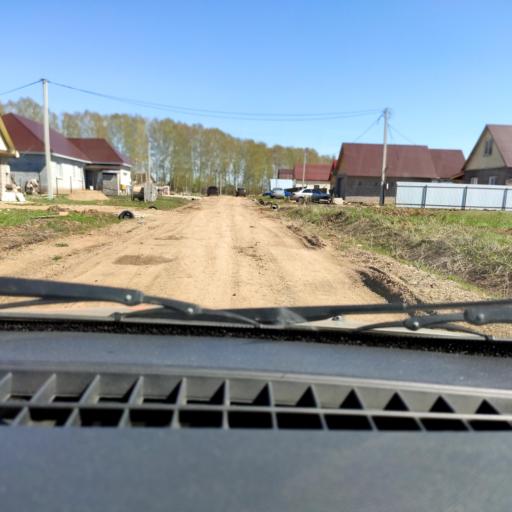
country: RU
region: Bashkortostan
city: Iglino
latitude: 54.8141
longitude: 56.4387
